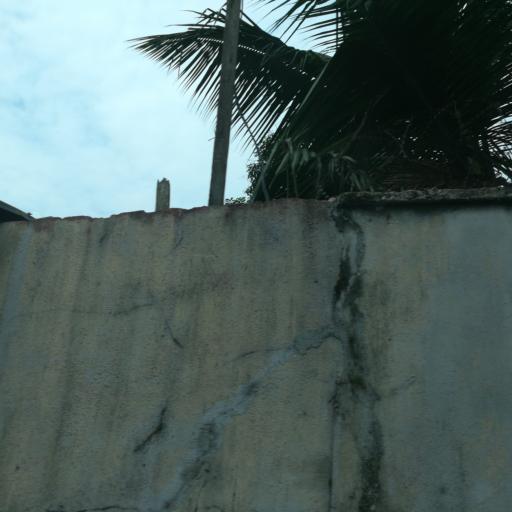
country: NG
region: Rivers
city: Port Harcourt
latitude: 4.8216
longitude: 6.9867
